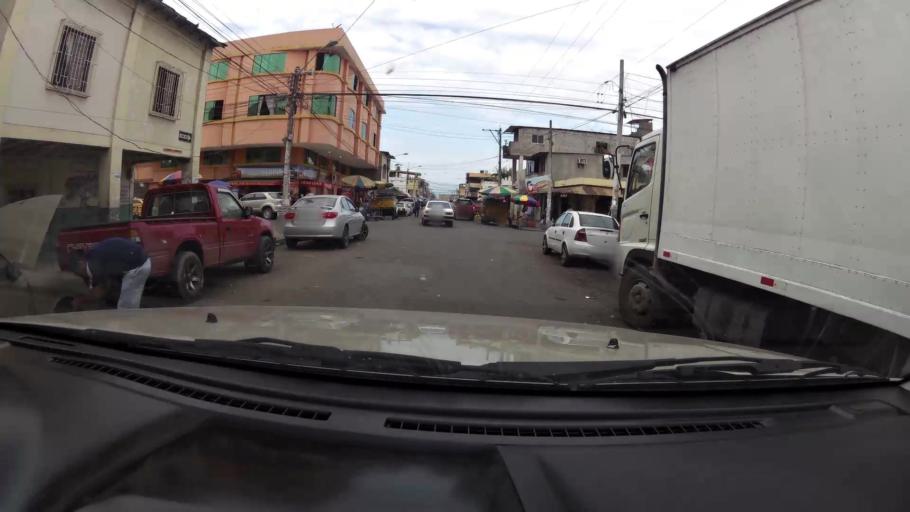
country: EC
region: El Oro
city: Machala
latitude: -3.2562
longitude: -79.9564
